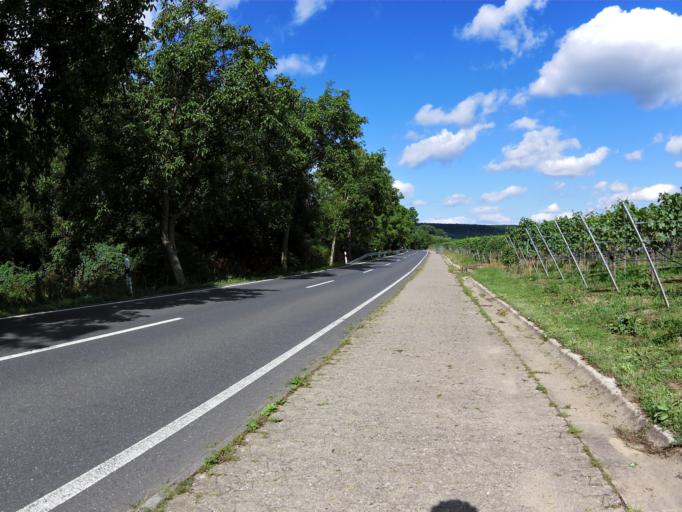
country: DE
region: Bavaria
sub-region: Regierungsbezirk Unterfranken
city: Sommerach
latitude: 49.8367
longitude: 10.1839
